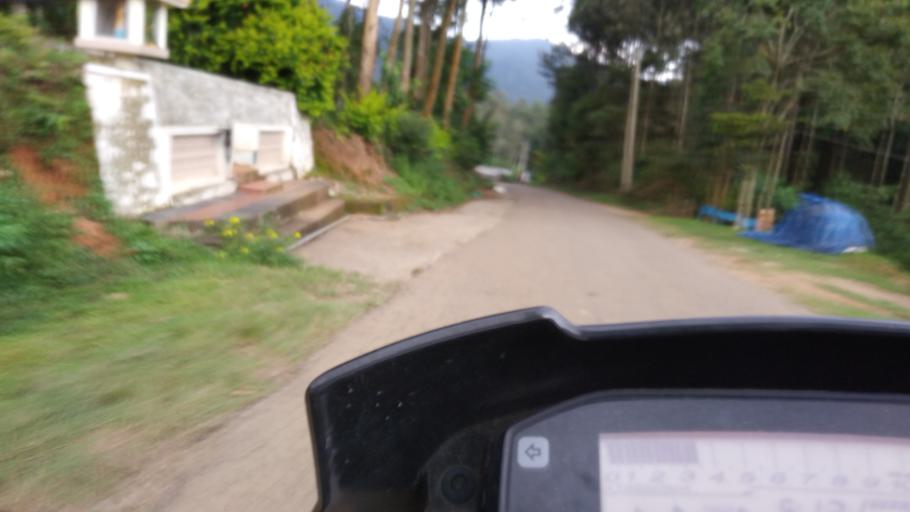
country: IN
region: Tamil Nadu
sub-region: Theni
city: Bodinayakkanur
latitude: 10.0234
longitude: 77.2414
